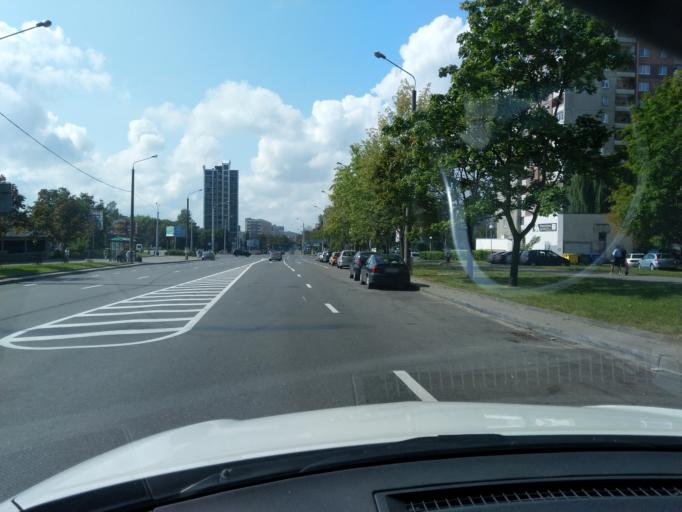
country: BY
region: Minsk
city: Minsk
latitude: 53.9299
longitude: 27.5869
